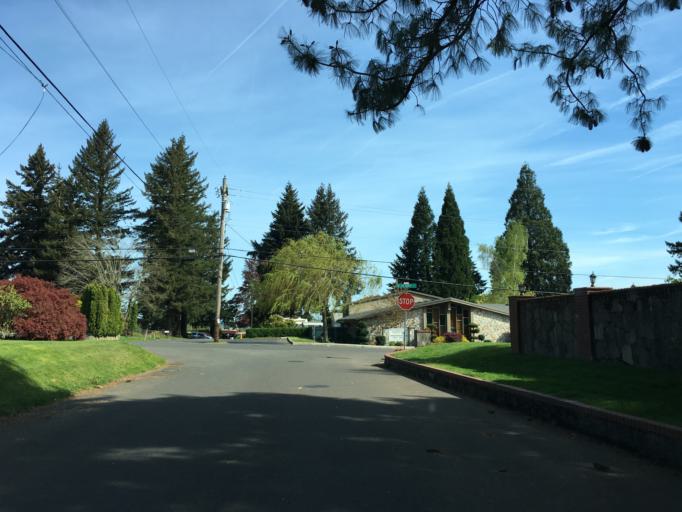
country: US
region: Oregon
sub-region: Multnomah County
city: Lents
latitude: 45.5370
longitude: -122.5192
